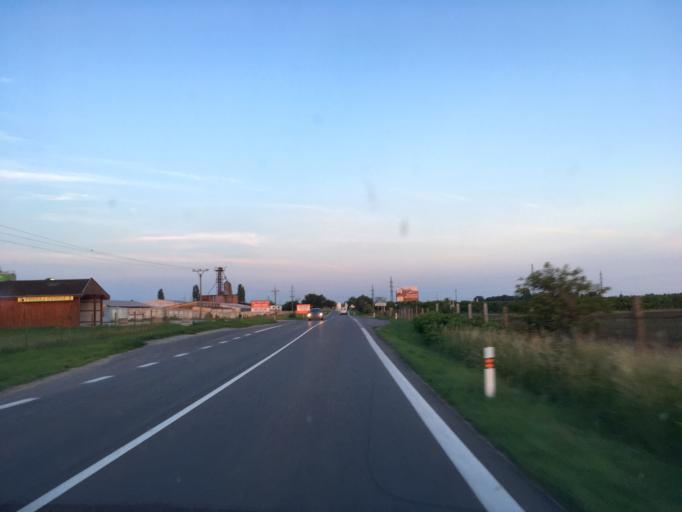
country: SK
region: Nitriansky
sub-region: Okres Nove Zamky
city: Nove Zamky
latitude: 48.0168
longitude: 18.1494
